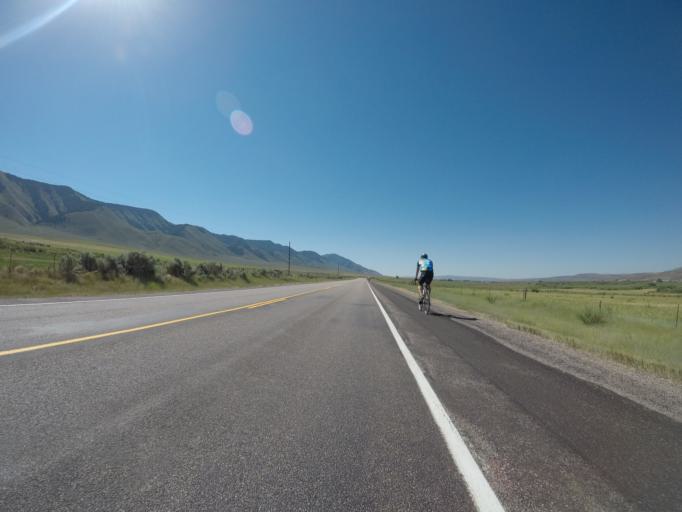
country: US
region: Idaho
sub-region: Bear Lake County
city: Montpelier
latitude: 42.3555
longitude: -111.0489
